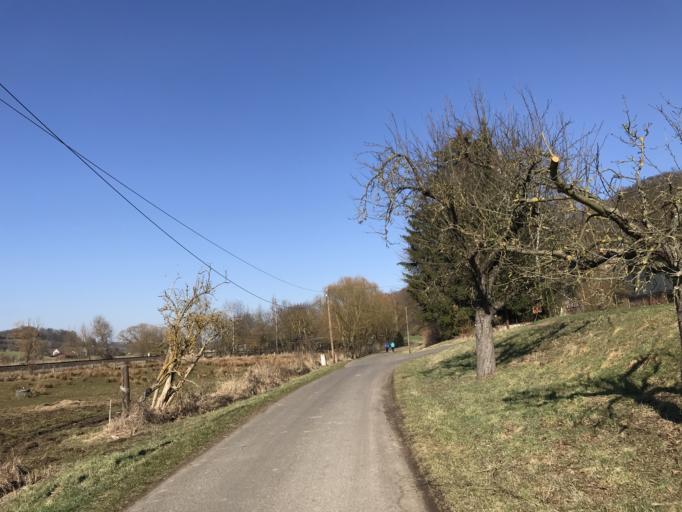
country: DE
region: Hesse
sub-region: Regierungsbezirk Darmstadt
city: Ranstadt
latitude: 50.3677
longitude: 8.9810
